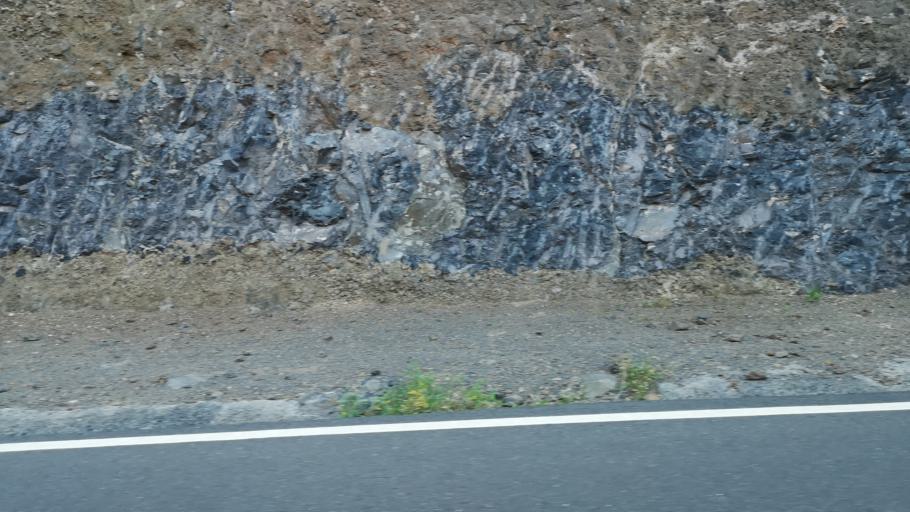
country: ES
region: Canary Islands
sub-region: Provincia de Santa Cruz de Tenerife
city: San Sebastian de la Gomera
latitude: 28.0850
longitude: -17.1234
